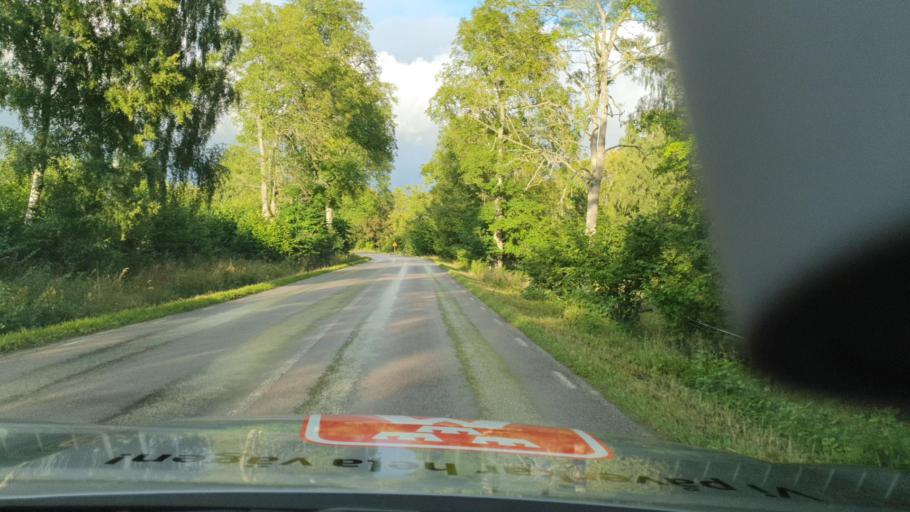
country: SE
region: Gotland
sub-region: Gotland
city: Klintehamn
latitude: 57.4202
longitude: 18.2295
